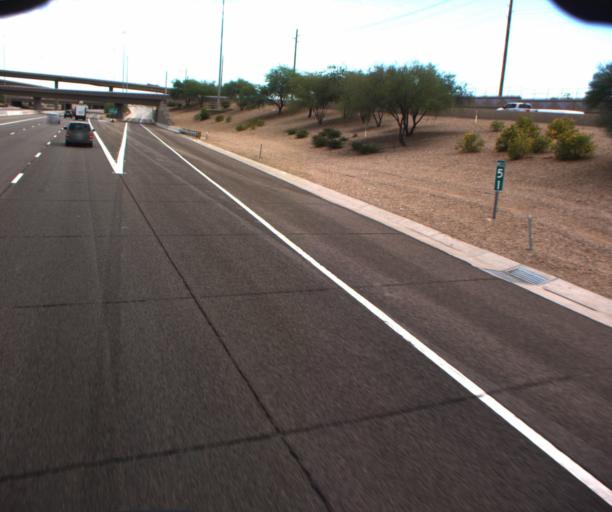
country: US
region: Arizona
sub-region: Maricopa County
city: Chandler
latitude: 33.2919
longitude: -111.8983
